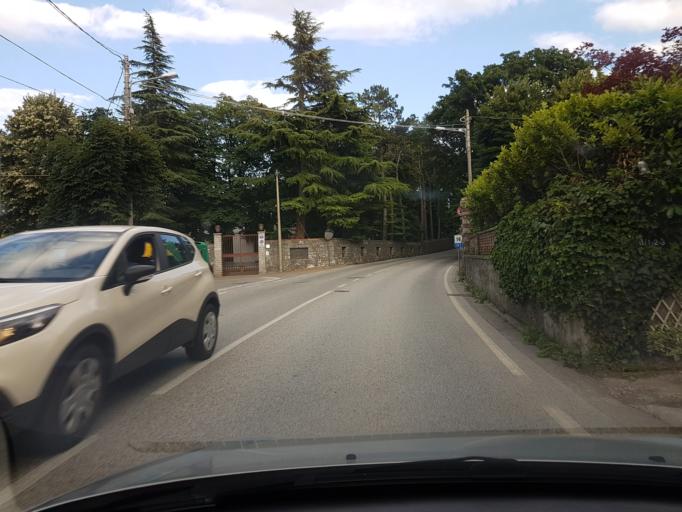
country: IT
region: Friuli Venezia Giulia
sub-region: Provincia di Trieste
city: Villa Opicina
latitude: 45.6877
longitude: 13.7924
